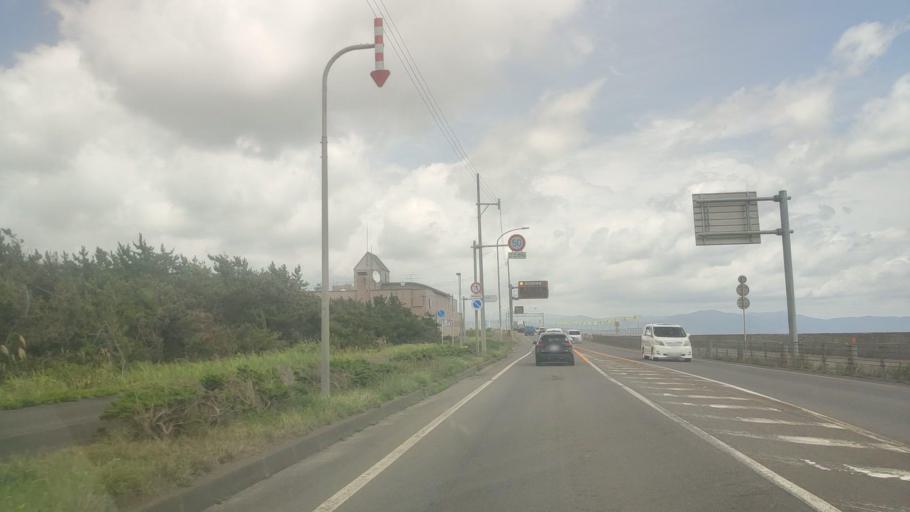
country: JP
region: Hokkaido
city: Niseko Town
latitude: 42.5121
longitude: 140.3796
